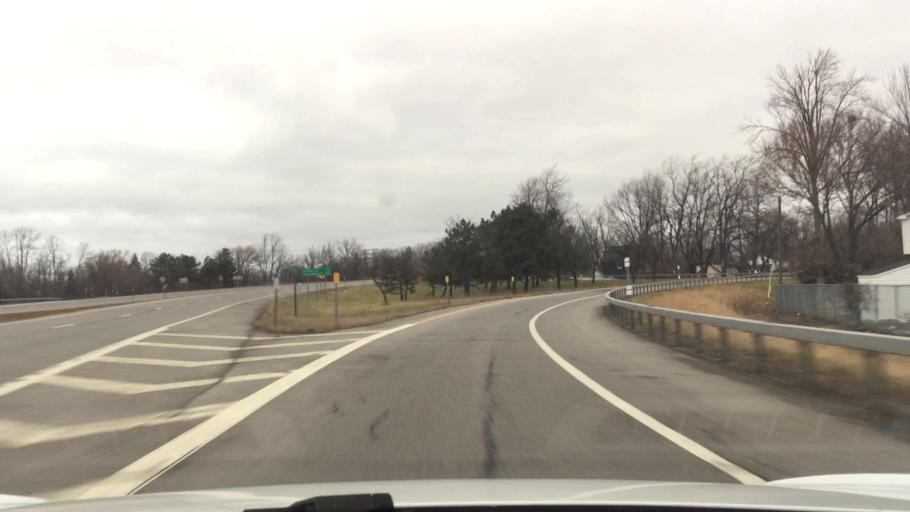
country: US
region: New York
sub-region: Erie County
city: Tonawanda
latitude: 43.0094
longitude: -78.8615
